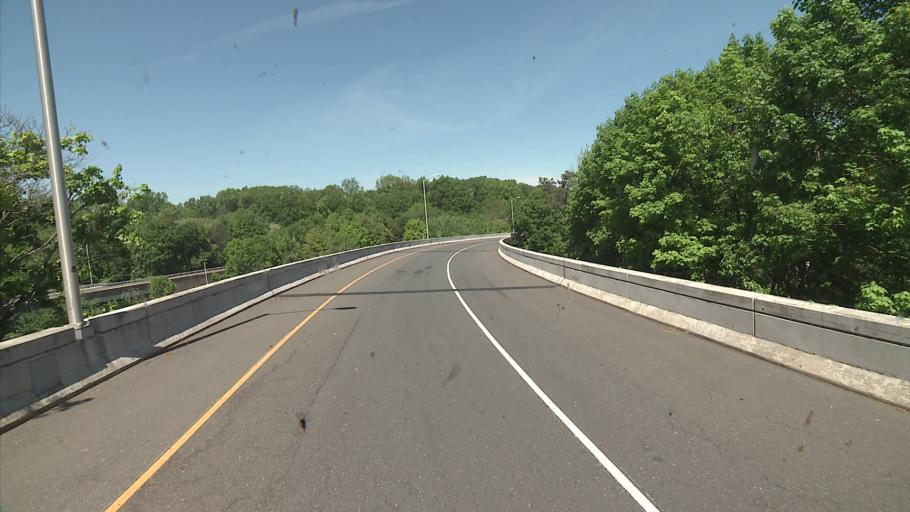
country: US
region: Connecticut
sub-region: Hartford County
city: West Hartford
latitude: 41.7495
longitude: -72.7339
